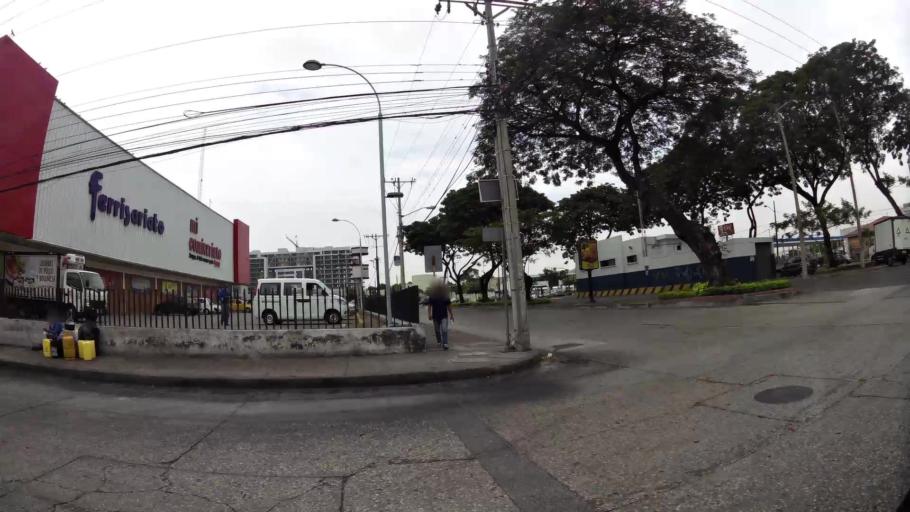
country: EC
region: Guayas
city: Eloy Alfaro
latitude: -2.1448
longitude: -79.8859
